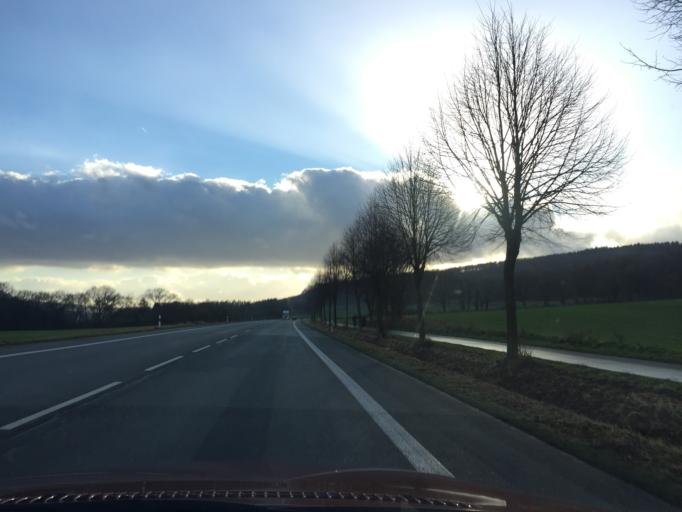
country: DE
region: North Rhine-Westphalia
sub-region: Regierungsbezirk Detmold
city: Hoexter
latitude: 51.8126
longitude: 9.4015
